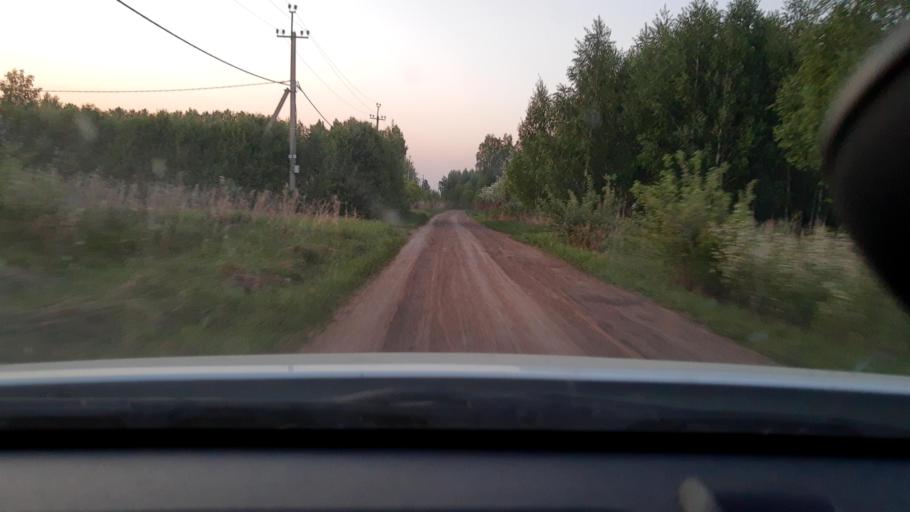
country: RU
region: Bashkortostan
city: Avdon
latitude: 54.5327
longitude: 55.8159
